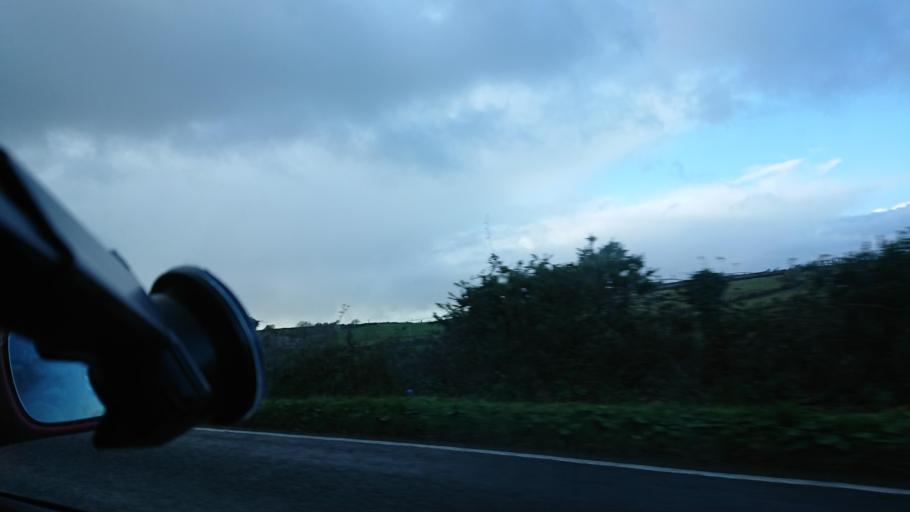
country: GB
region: England
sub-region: Cornwall
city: Looe
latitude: 50.3510
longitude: -4.4760
